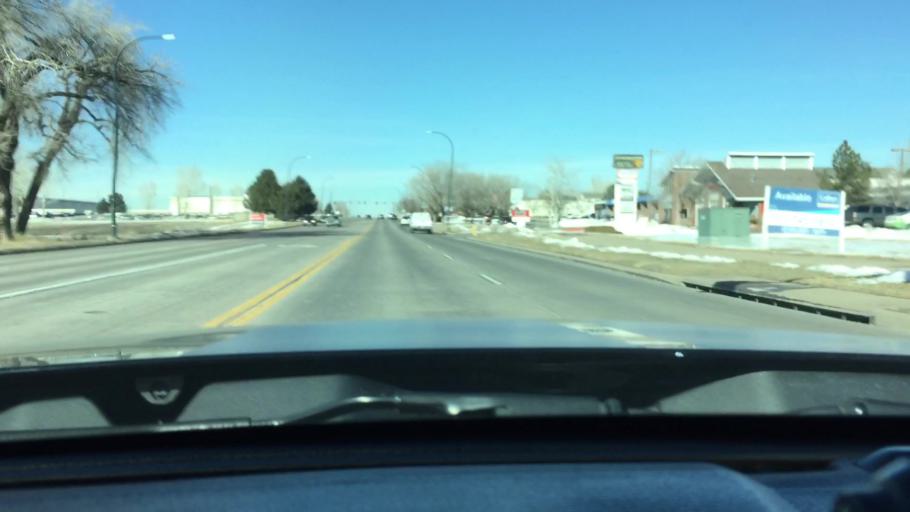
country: US
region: Colorado
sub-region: Adams County
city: Northglenn
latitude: 39.9035
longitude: -104.9967
